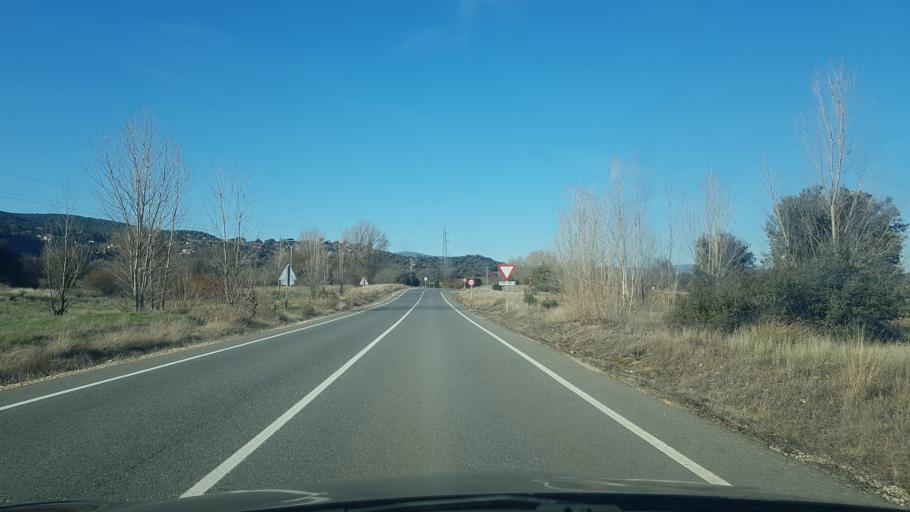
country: ES
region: Madrid
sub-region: Provincia de Madrid
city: San Martin de Valdeiglesias
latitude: 40.3728
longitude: -4.4439
